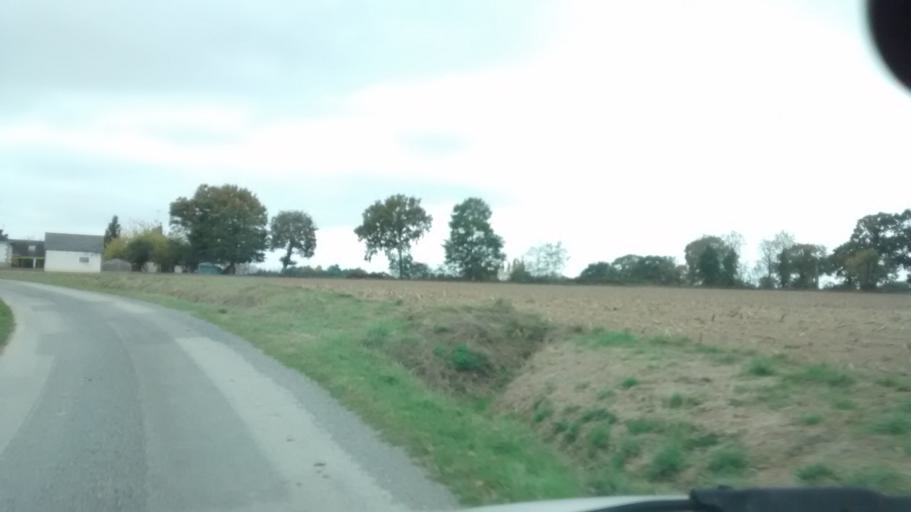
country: FR
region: Brittany
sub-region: Departement d'Ille-et-Vilaine
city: Noyal-sur-Vilaine
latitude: 48.1257
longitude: -1.5095
